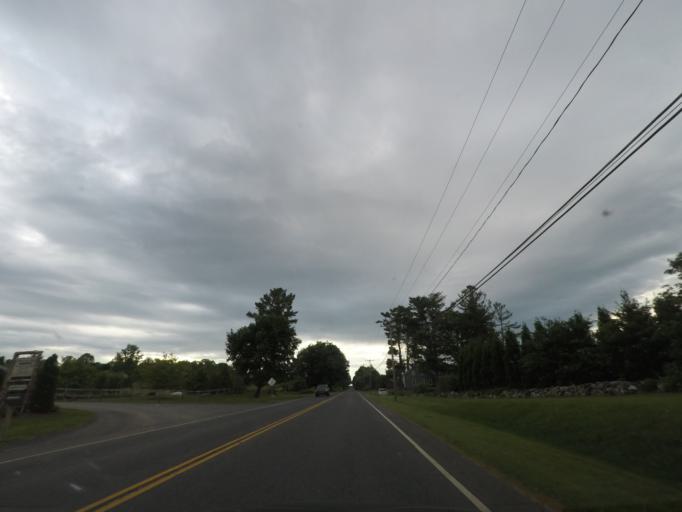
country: US
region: Connecticut
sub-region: Litchfield County
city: Canaan
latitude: 41.9290
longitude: -73.4182
